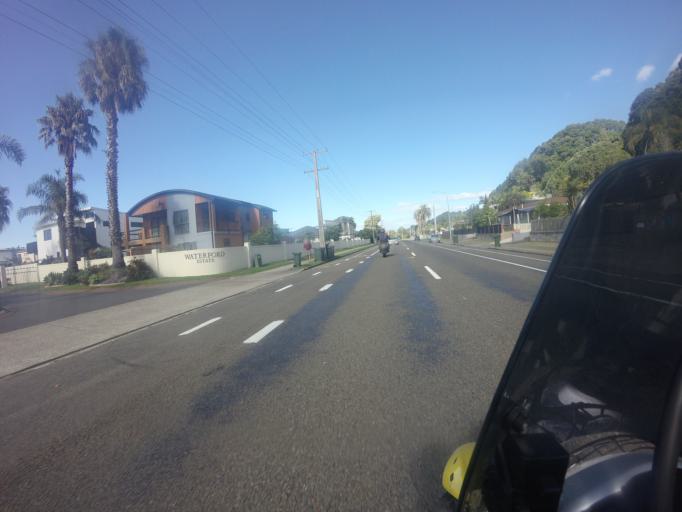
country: NZ
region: Bay of Plenty
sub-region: Whakatane District
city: Whakatane
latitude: -37.9703
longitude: 177.0539
